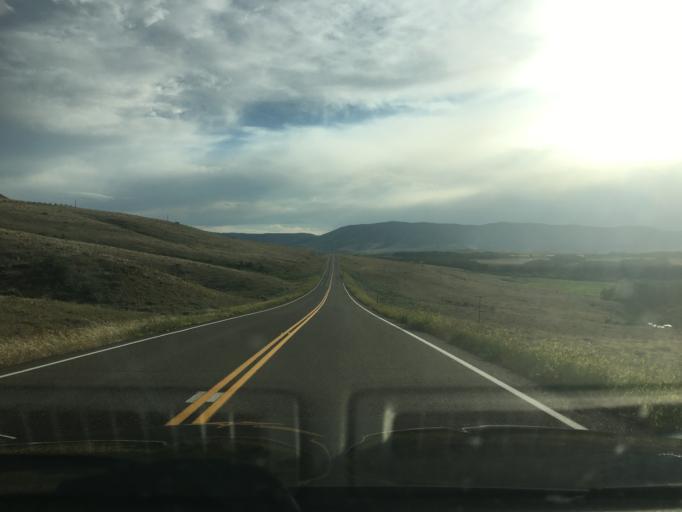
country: US
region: Wyoming
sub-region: Albany County
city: Laramie
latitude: 41.2856
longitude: -106.0494
